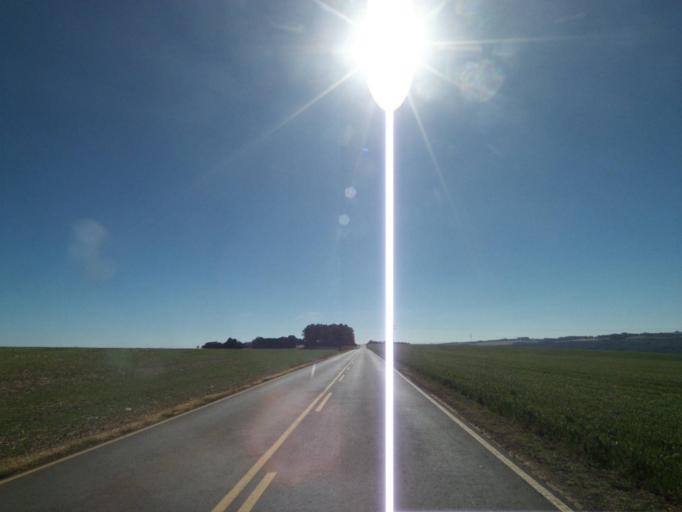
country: BR
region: Parana
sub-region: Tibagi
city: Tibagi
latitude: -24.5593
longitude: -50.2905
